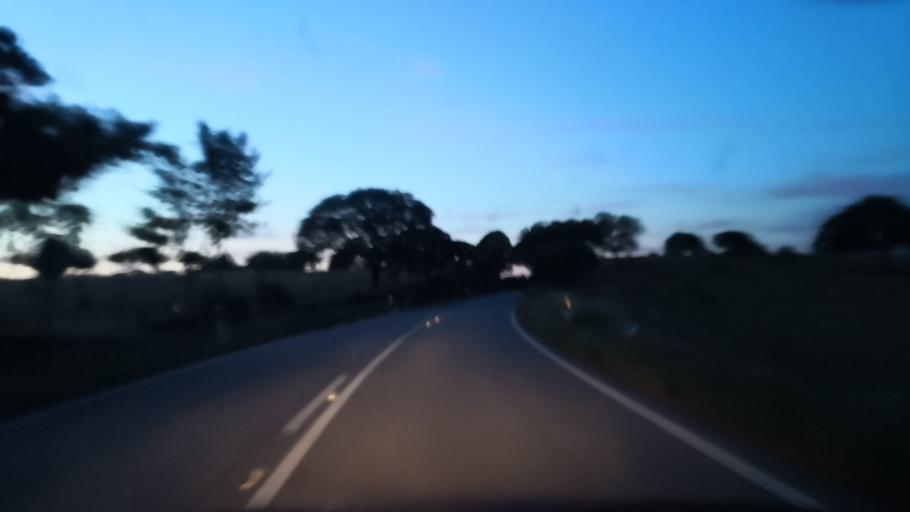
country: ES
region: Extremadura
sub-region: Provincia de Caceres
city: Piedras Albas
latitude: 39.8477
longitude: -6.9817
